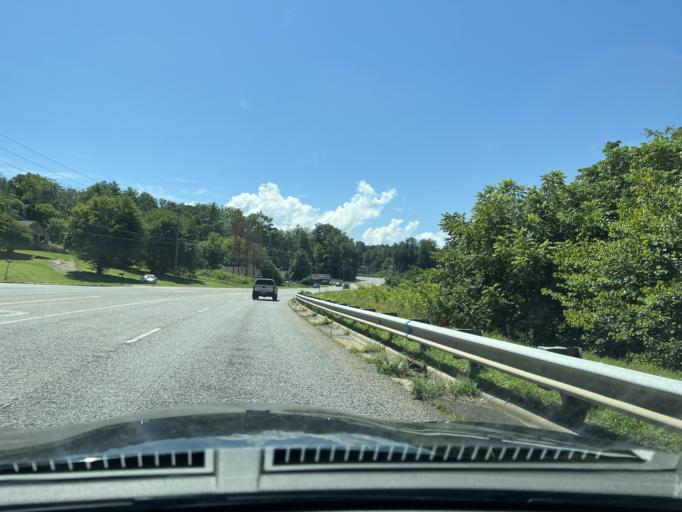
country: US
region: North Carolina
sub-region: Buncombe County
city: Fairview
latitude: 35.5296
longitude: -82.4270
